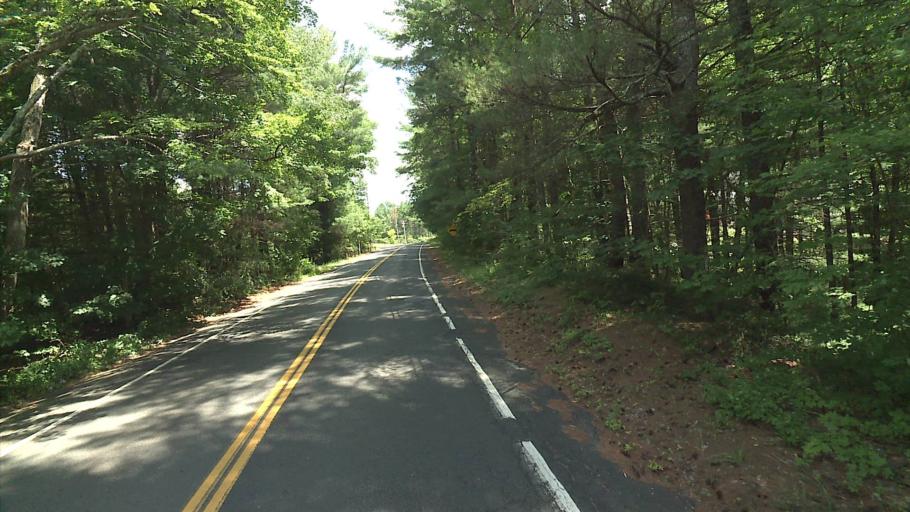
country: US
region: Connecticut
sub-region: Litchfield County
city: Winsted
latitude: 41.9878
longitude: -73.1161
